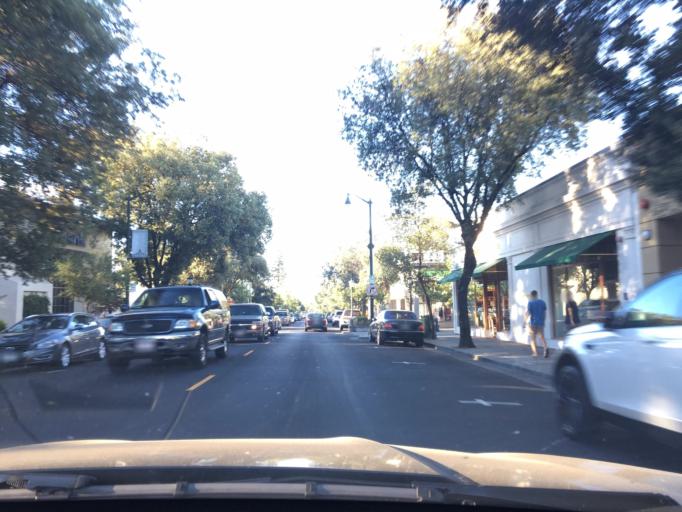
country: US
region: California
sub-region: Santa Clara County
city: Los Gatos
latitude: 37.2248
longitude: -121.9828
